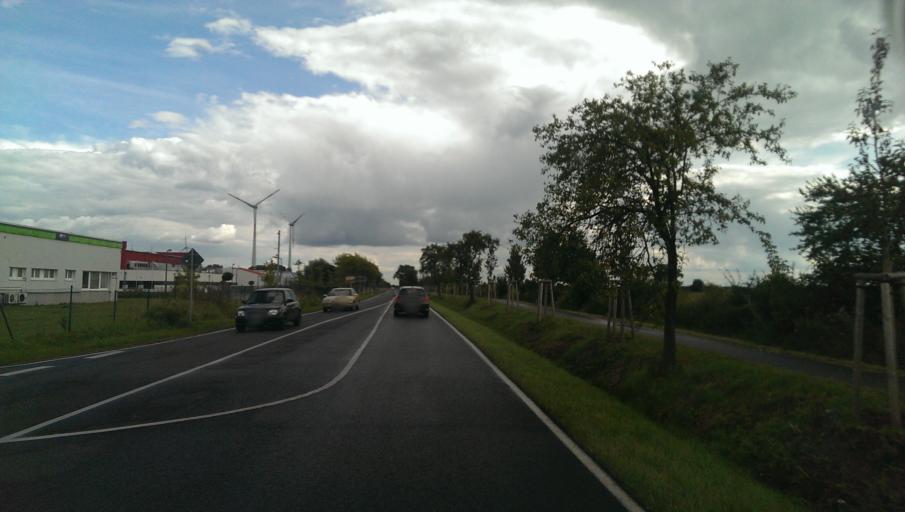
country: DE
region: Brandenburg
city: Velten
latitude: 52.6913
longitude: 13.1161
